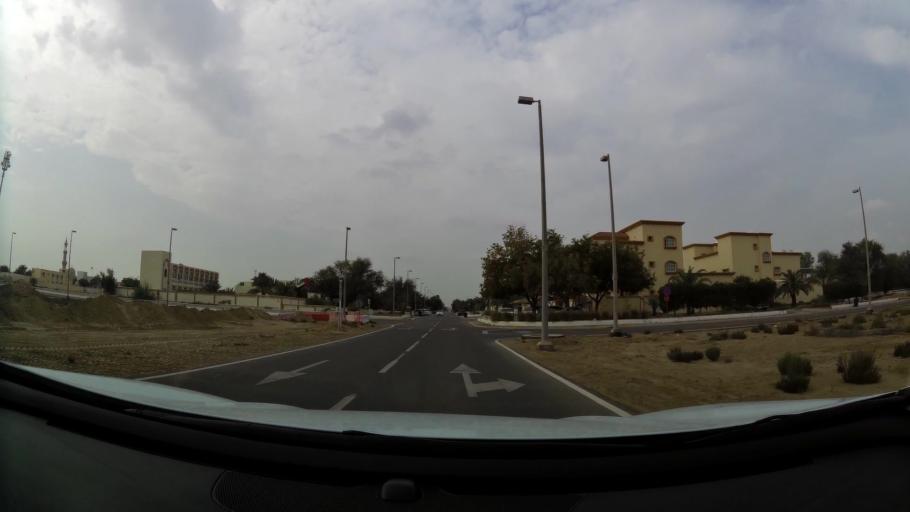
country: AE
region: Abu Dhabi
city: Abu Dhabi
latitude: 24.6349
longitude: 54.7211
